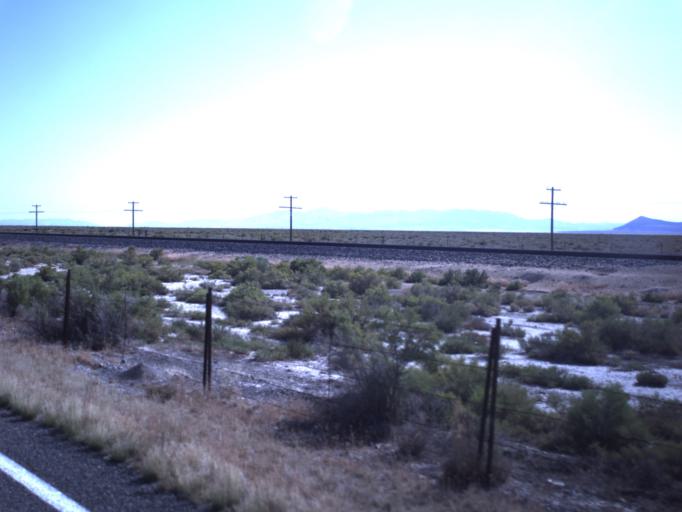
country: US
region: Utah
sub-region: Millard County
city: Delta
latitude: 39.0847
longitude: -112.7537
